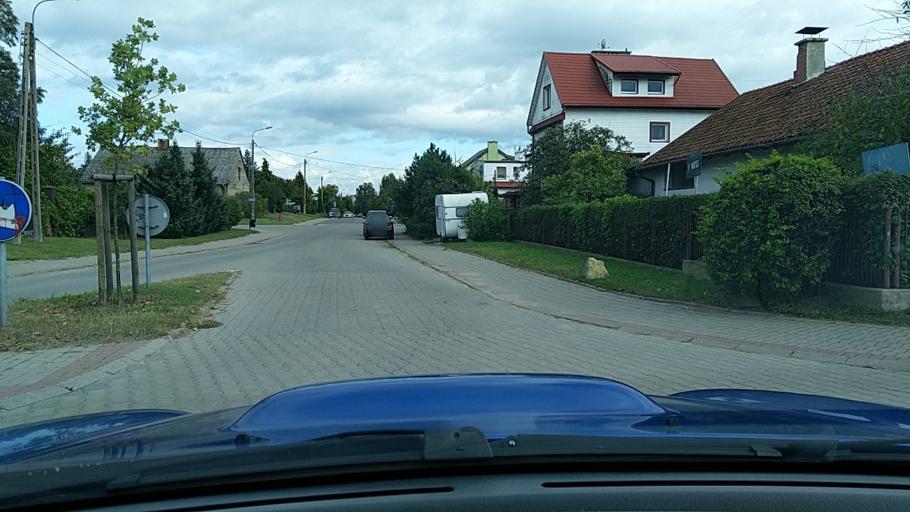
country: PL
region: Warmian-Masurian Voivodeship
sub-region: Olsztyn
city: Kortowo
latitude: 53.7663
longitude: 20.4227
